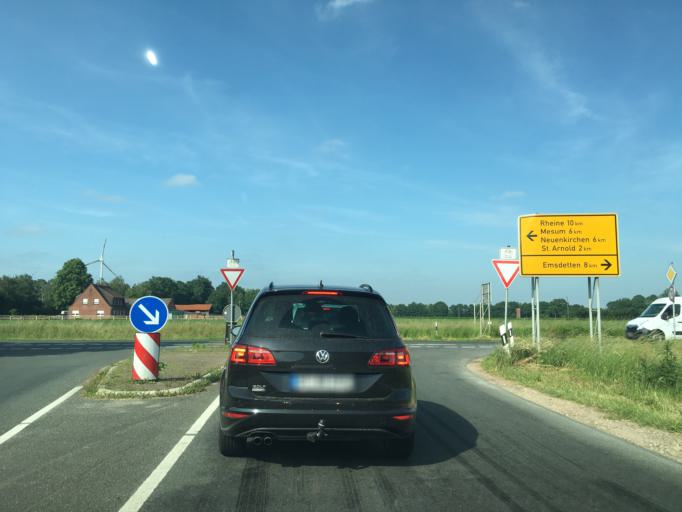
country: DE
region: North Rhine-Westphalia
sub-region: Regierungsbezirk Munster
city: Neuenkirchen
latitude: 52.1924
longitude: 7.4185
